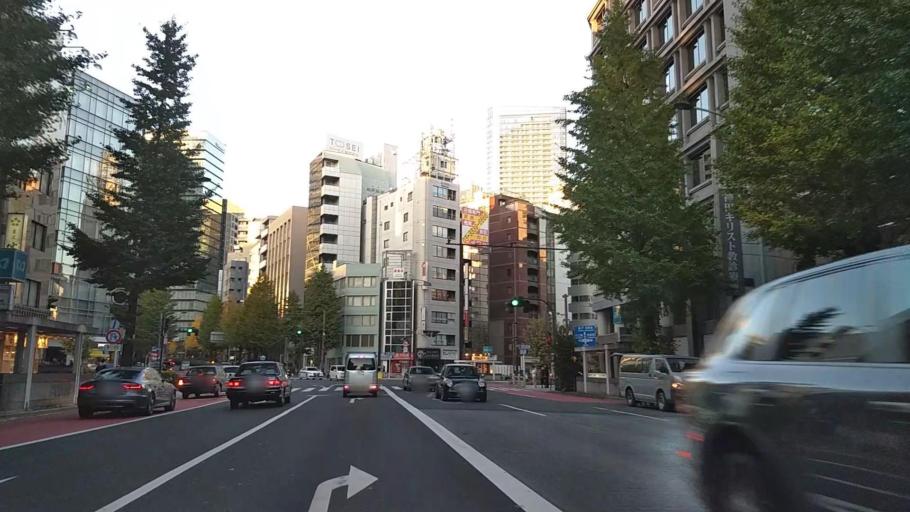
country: JP
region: Tokyo
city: Tokyo
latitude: 35.6940
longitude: 139.7653
